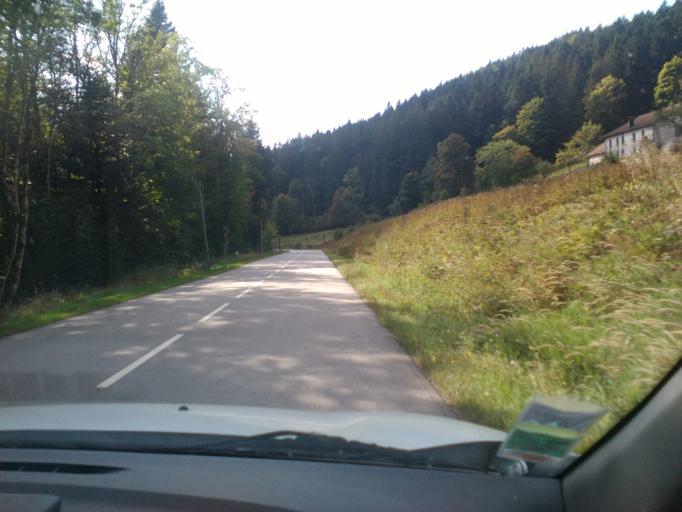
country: FR
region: Lorraine
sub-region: Departement des Vosges
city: Gerardmer
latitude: 48.0421
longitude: 6.8620
